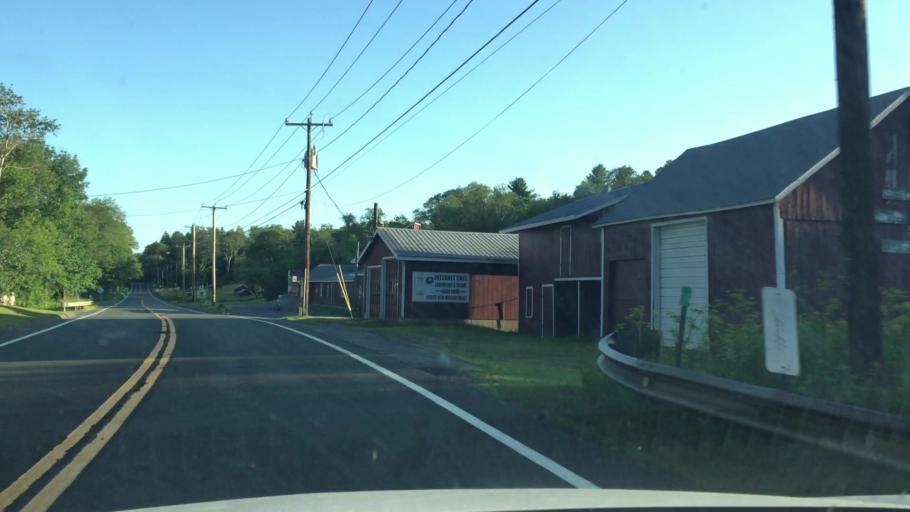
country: US
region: Massachusetts
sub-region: Berkshire County
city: Otis
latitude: 42.2319
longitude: -73.1098
